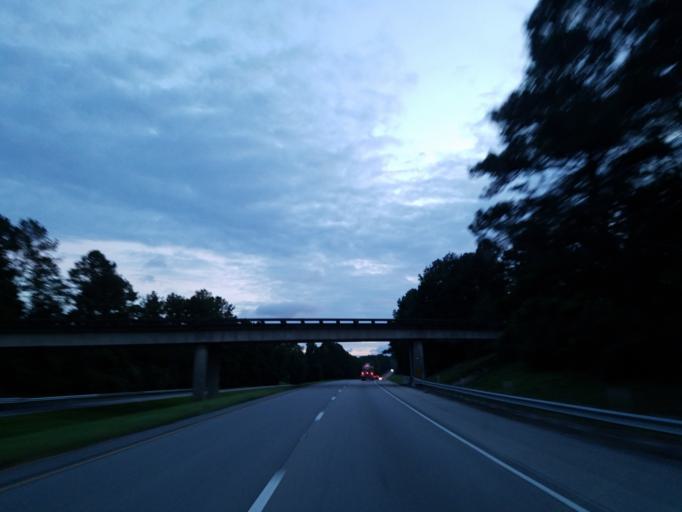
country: US
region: Mississippi
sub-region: Clarke County
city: Stonewall
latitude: 32.1911
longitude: -88.8532
